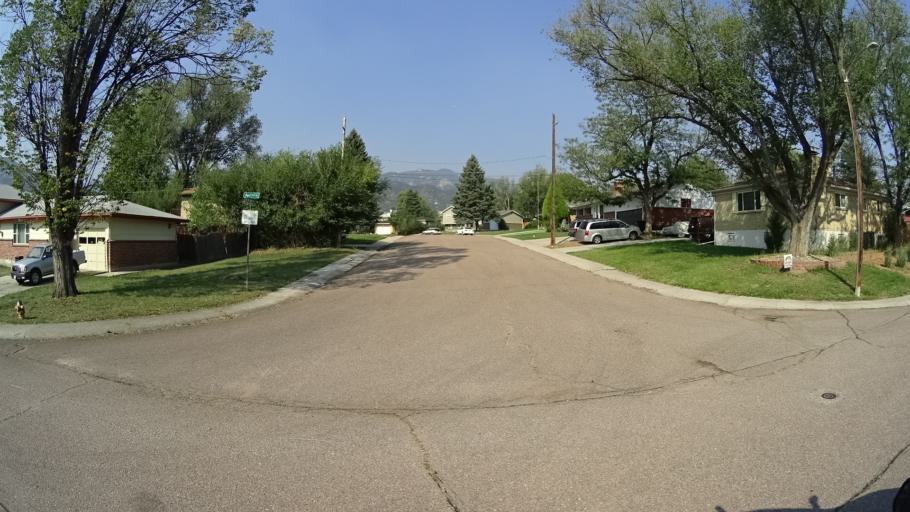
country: US
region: Colorado
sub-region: El Paso County
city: Colorado Springs
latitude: 38.8075
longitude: -104.8366
